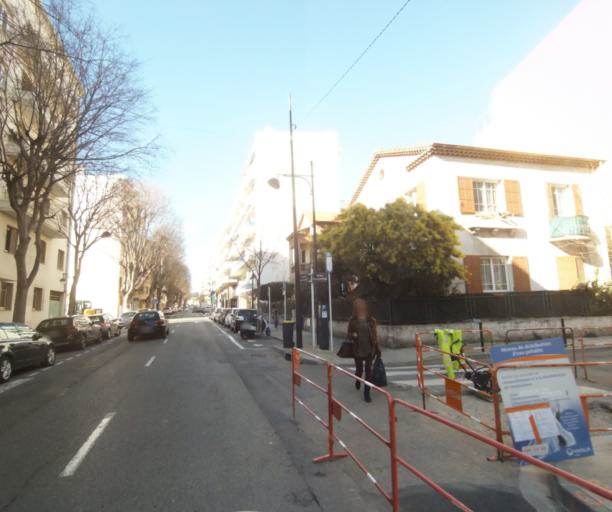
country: FR
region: Provence-Alpes-Cote d'Azur
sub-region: Departement des Alpes-Maritimes
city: Antibes
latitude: 43.5770
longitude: 7.1233
